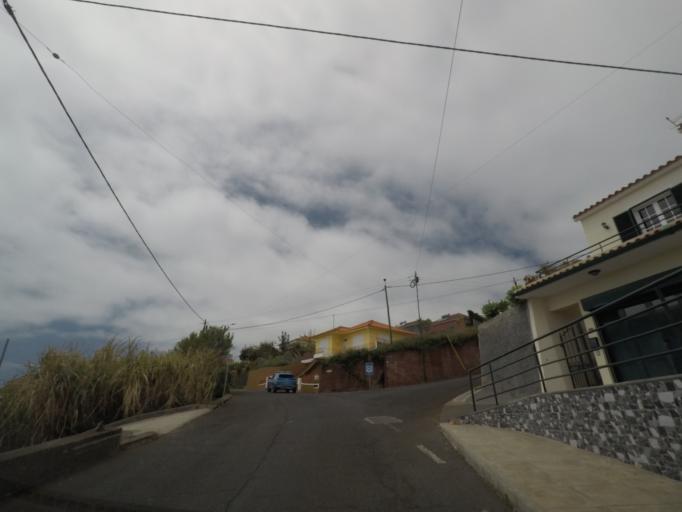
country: PT
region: Madeira
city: Ponta do Sol
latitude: 32.6953
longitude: -17.0978
